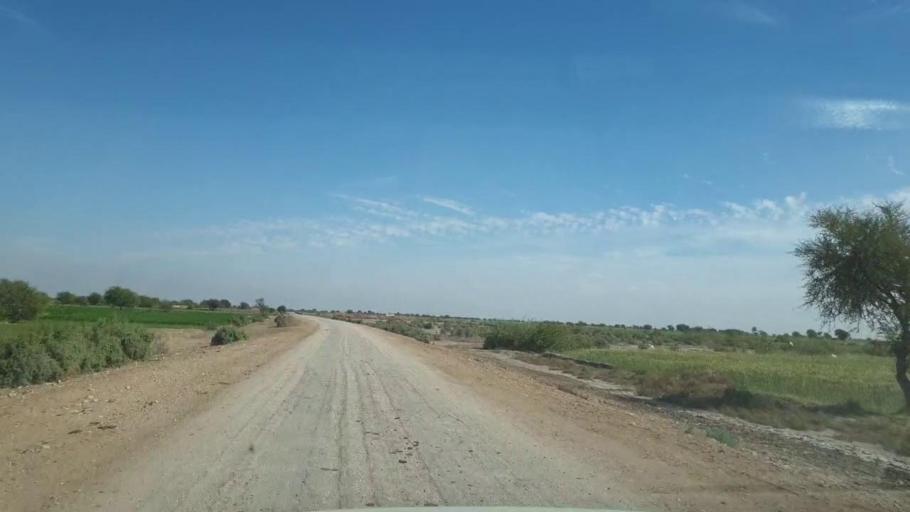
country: PK
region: Sindh
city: Pithoro
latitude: 25.5789
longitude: 69.2941
